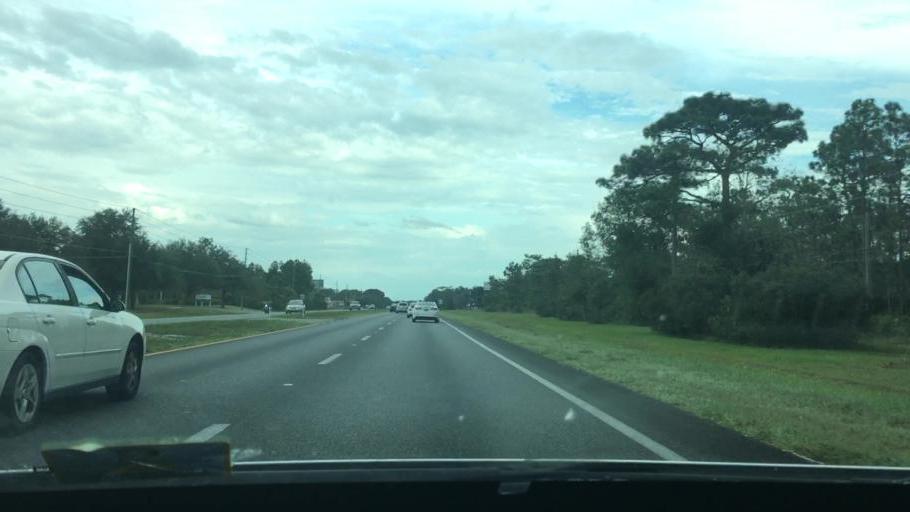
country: US
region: Florida
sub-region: Orange County
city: Bithlo
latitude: 28.5572
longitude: -81.1186
